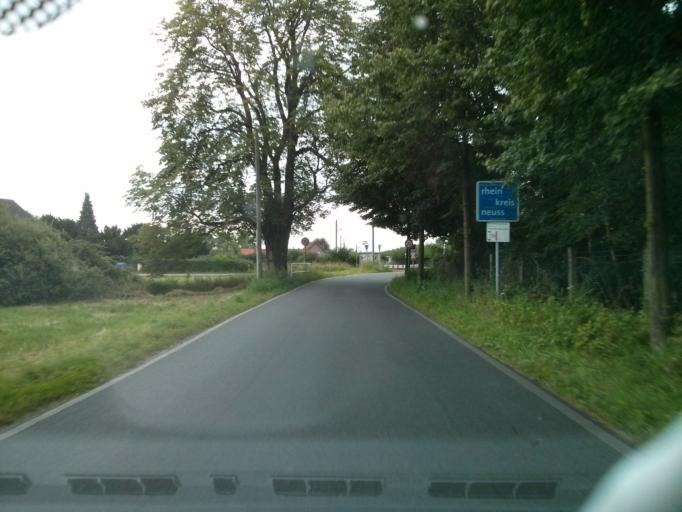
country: DE
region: North Rhine-Westphalia
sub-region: Regierungsbezirk Dusseldorf
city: Krefeld
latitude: 51.2971
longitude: 6.6190
